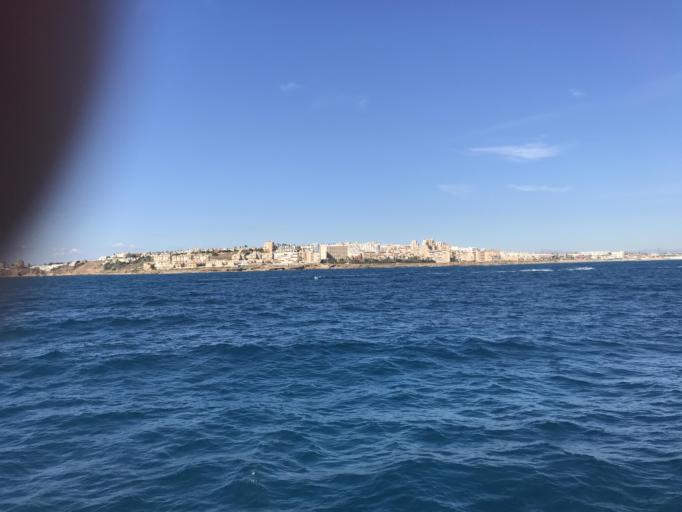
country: ES
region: Valencia
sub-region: Provincia de Alicante
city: Torrevieja
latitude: 38.0010
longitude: -0.6371
